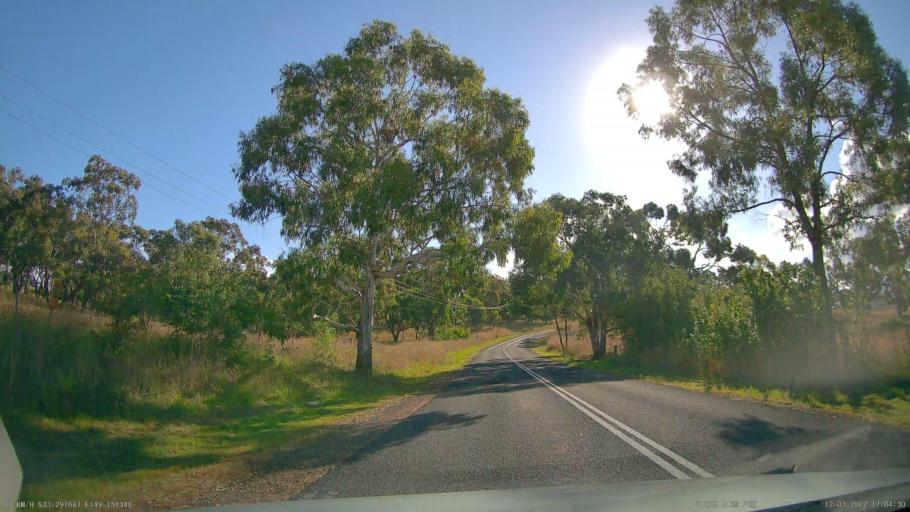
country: AU
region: New South Wales
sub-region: Orange Municipality
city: Orange
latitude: -33.2917
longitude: 149.1312
